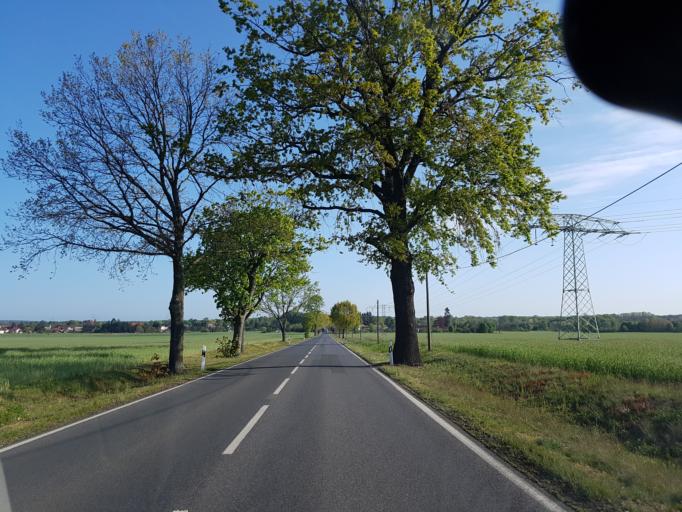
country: DE
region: Brandenburg
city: Altdobern
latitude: 51.6401
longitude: 14.0329
